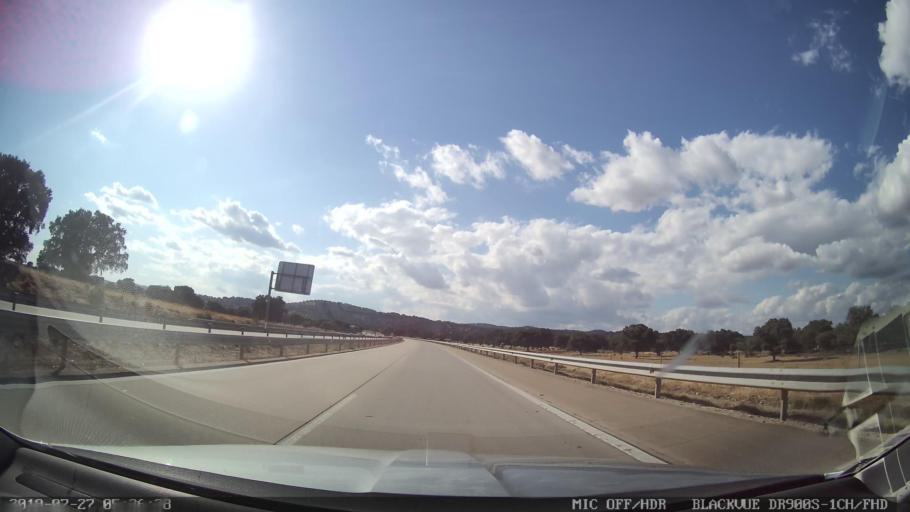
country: ES
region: Castille-La Mancha
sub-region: Province of Toledo
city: Cervera de los Montes
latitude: 40.0166
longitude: -4.7872
